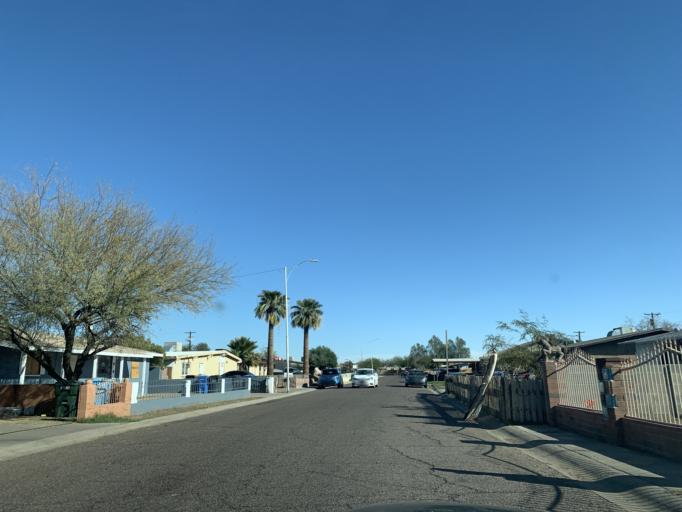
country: US
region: Arizona
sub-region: Maricopa County
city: Laveen
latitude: 33.3978
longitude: -112.1359
